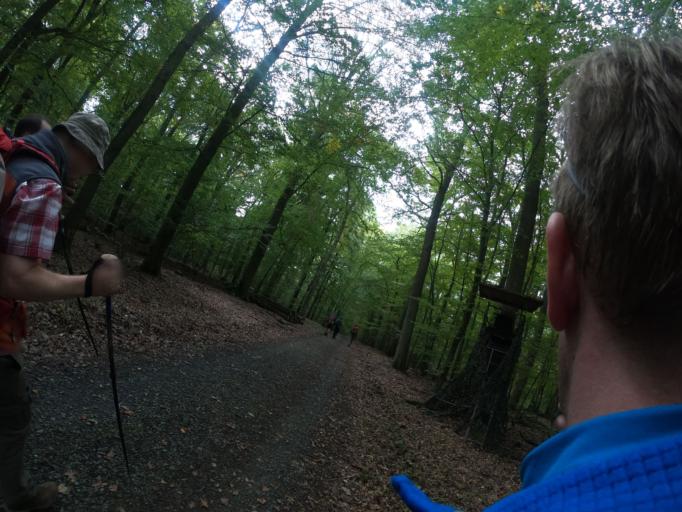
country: DE
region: Hesse
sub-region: Regierungsbezirk Darmstadt
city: Idstein
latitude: 50.2284
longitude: 8.2413
